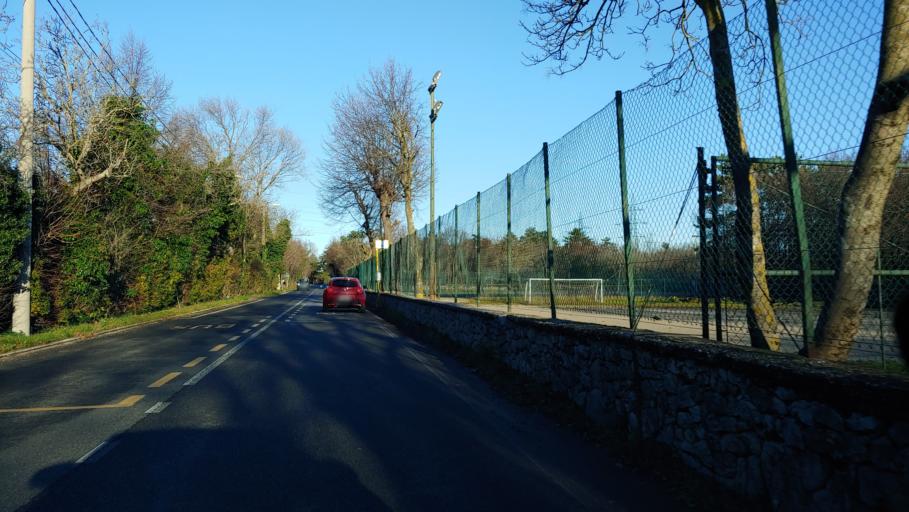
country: IT
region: Friuli Venezia Giulia
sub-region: Provincia di Trieste
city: Trieste
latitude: 45.6631
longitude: 13.8342
